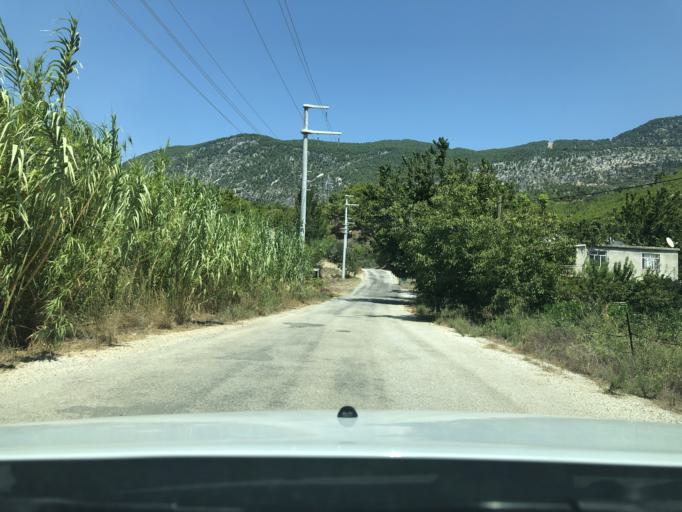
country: TR
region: Antalya
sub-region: Manavgat
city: Kizilagac
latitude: 36.8601
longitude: 31.5635
